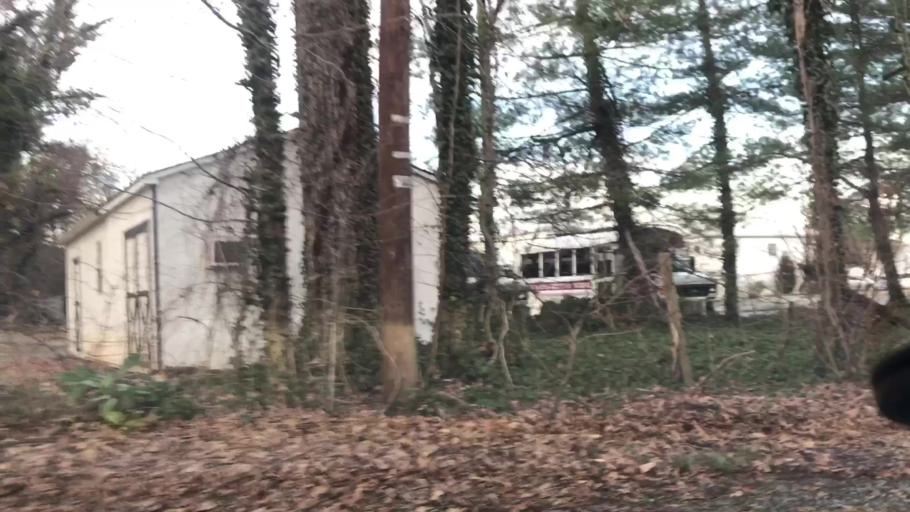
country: US
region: Virginia
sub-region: City of Charlottesville
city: Charlottesville
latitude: 38.0411
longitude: -78.5154
